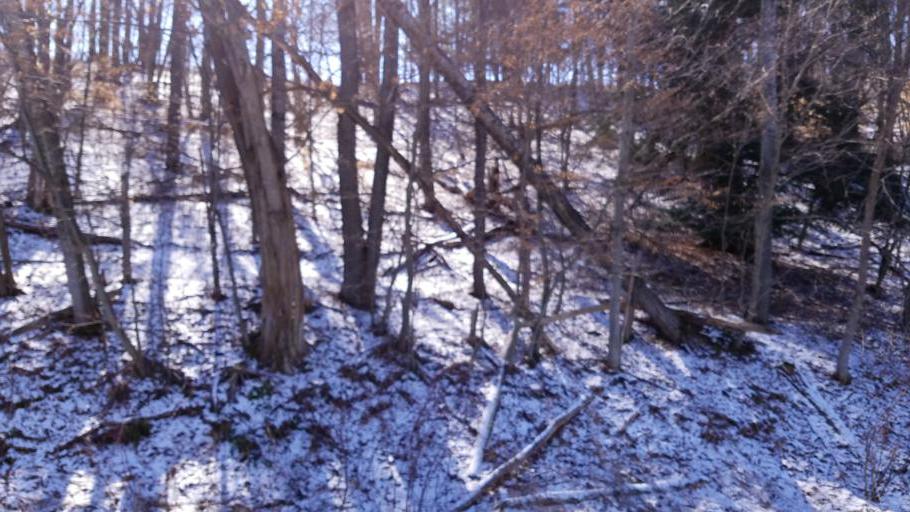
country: US
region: New York
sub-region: Allegany County
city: Wellsville
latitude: 42.0738
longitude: -77.9294
